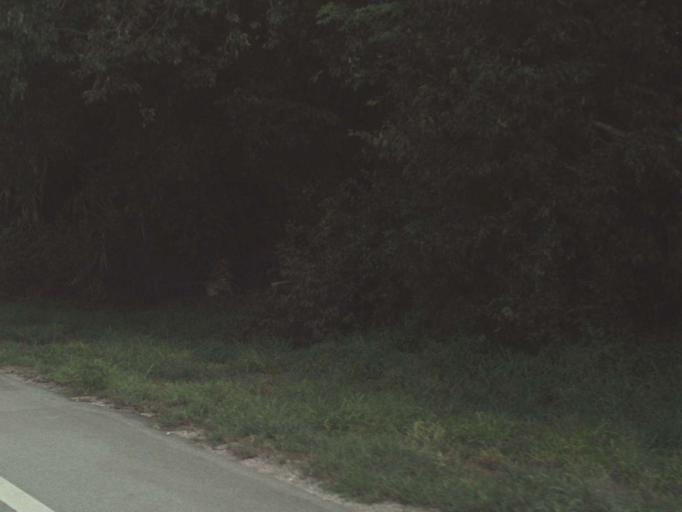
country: US
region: Florida
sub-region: Martin County
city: Indiantown
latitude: 27.0451
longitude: -80.6405
